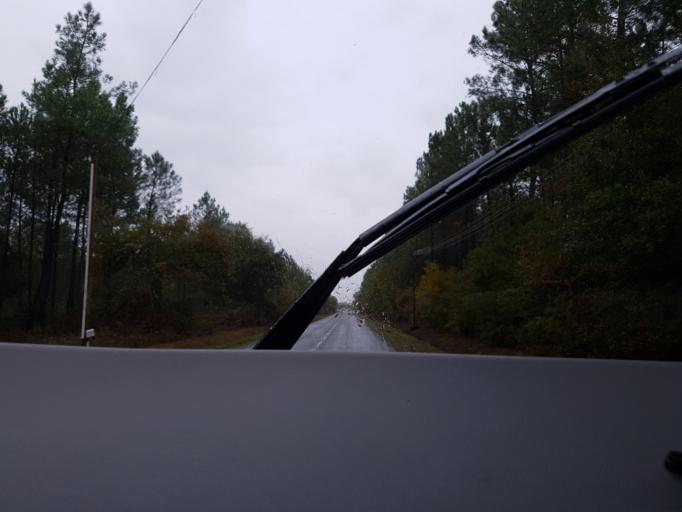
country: FR
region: Aquitaine
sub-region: Departement de la Gironde
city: Saint-Symphorien
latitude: 44.3358
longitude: -0.5983
